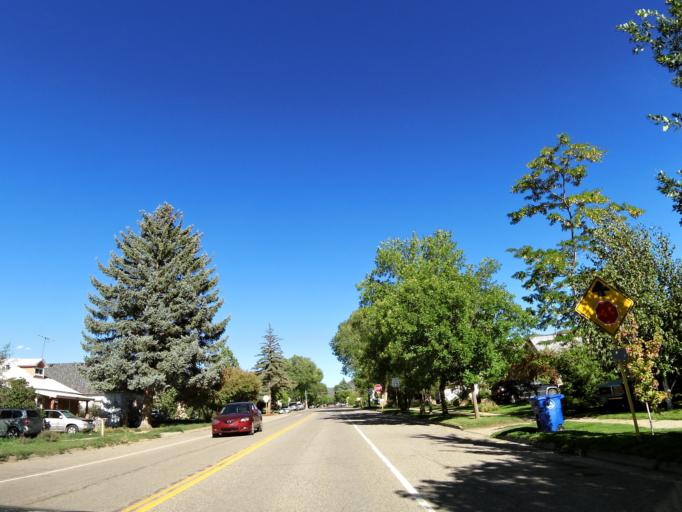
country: US
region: Colorado
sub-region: Montezuma County
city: Mancos
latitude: 37.3450
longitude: -108.2970
